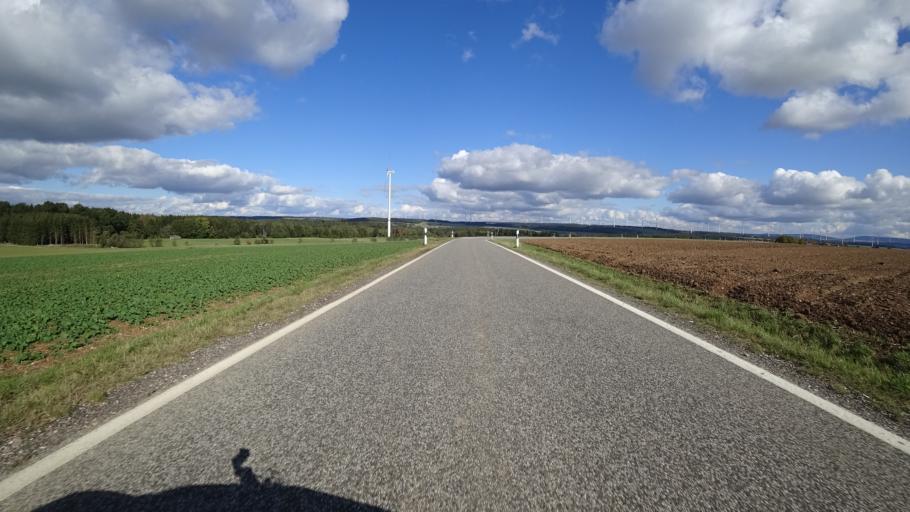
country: DE
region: Rheinland-Pfalz
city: Michelbach
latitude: 50.0160
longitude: 7.4382
